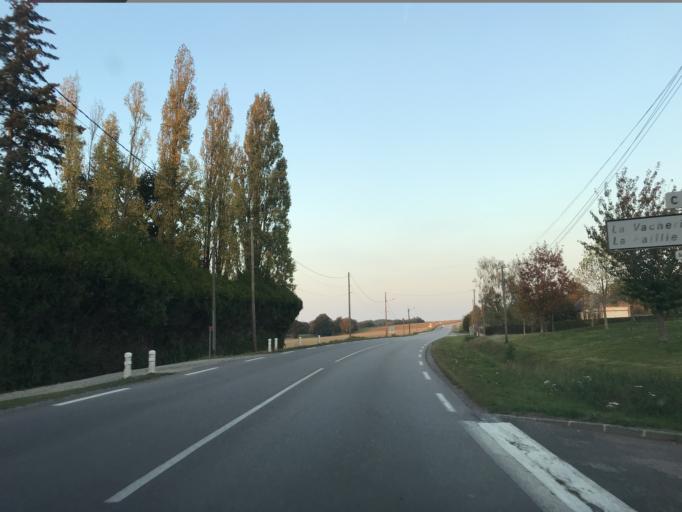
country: FR
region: Haute-Normandie
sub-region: Departement de l'Eure
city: Bourth
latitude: 48.6866
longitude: 0.8108
